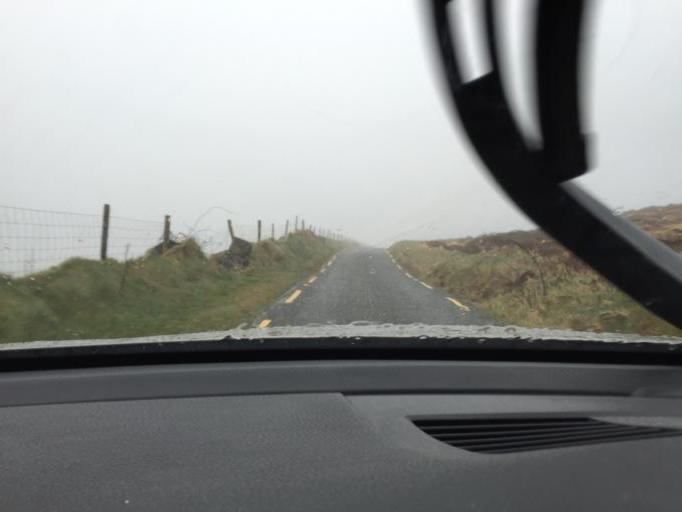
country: IE
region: Munster
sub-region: Ciarrai
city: Dingle
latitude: 52.1365
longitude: -10.4422
